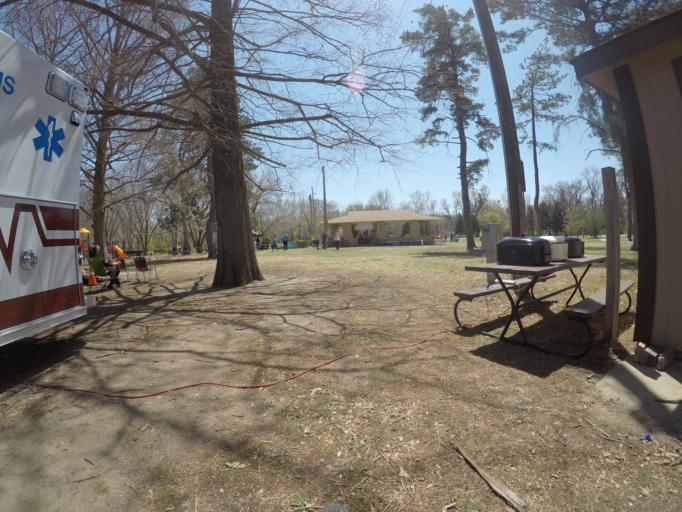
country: US
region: Kansas
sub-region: Pratt County
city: Pratt
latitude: 37.6349
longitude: -98.7344
